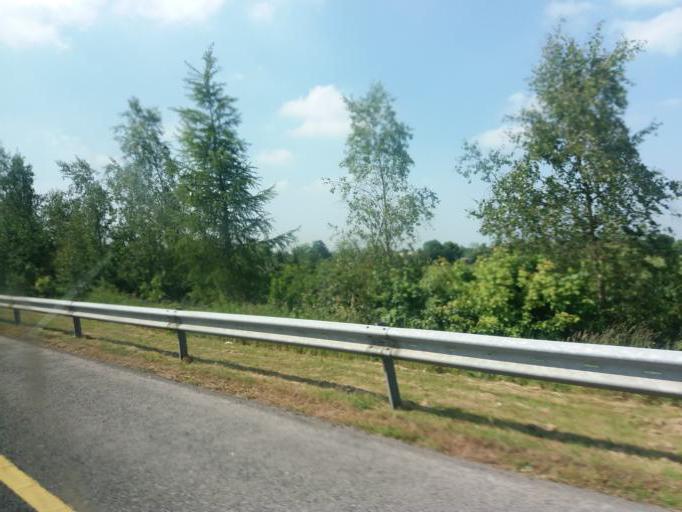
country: IE
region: Leinster
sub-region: An Mhi
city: Ashbourne
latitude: 53.5064
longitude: -6.4199
